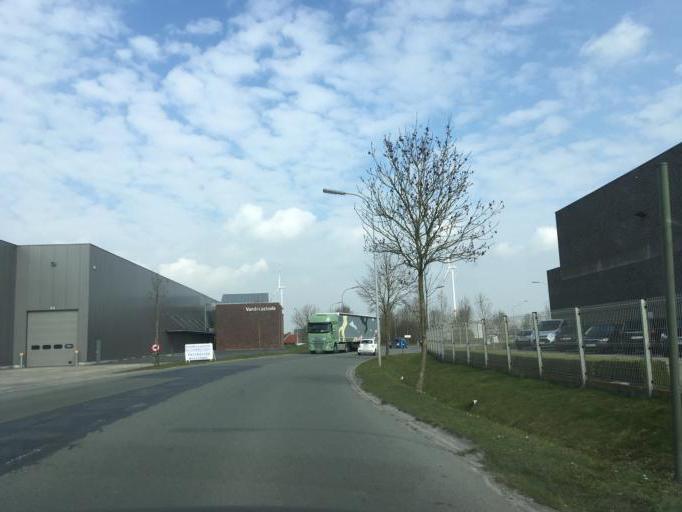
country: BE
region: Flanders
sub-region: Provincie West-Vlaanderen
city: Izegem
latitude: 50.9263
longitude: 3.1773
